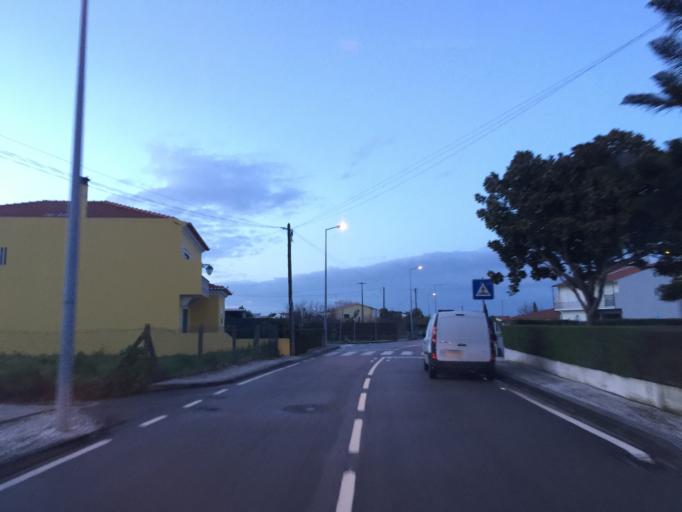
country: PT
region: Coimbra
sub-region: Figueira da Foz
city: Lavos
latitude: 40.0702
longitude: -8.8026
